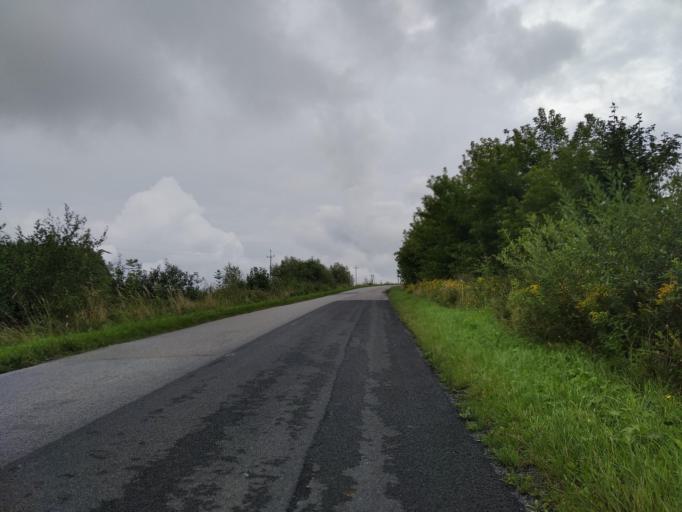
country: PL
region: Subcarpathian Voivodeship
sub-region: Powiat rzeszowski
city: Dynow
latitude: 49.7218
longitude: 22.3157
